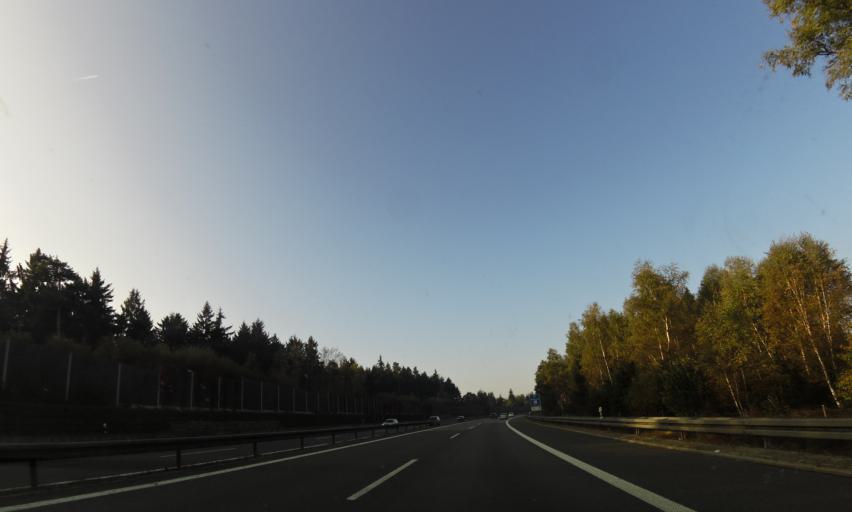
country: DE
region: Saxony
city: Waldkirchen
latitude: 50.6108
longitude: 12.4046
